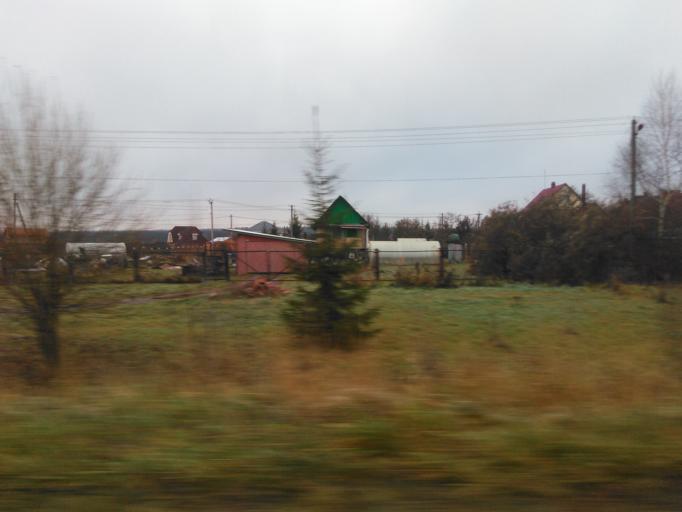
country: RU
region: Moskovskaya
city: Ashukino
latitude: 56.1725
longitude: 37.9395
